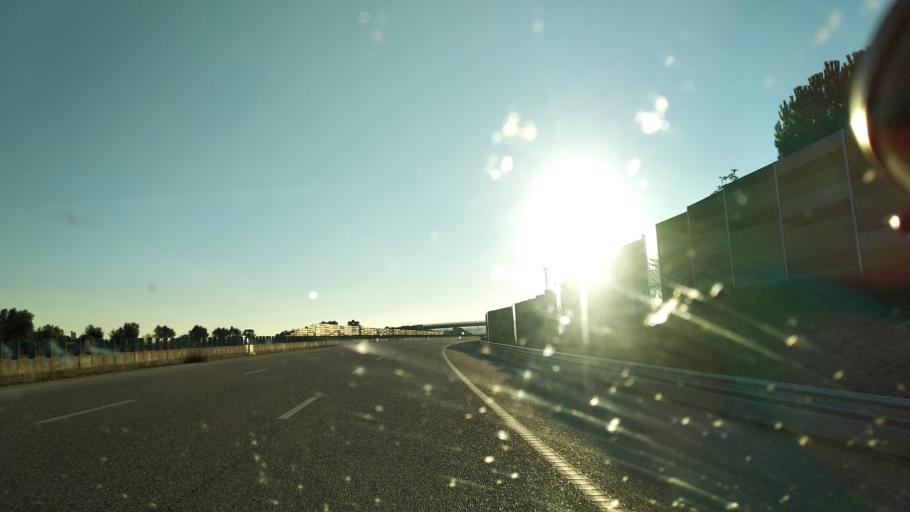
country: PT
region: Santarem
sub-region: Alcanena
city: Alcanena
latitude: 39.3623
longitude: -8.6321
